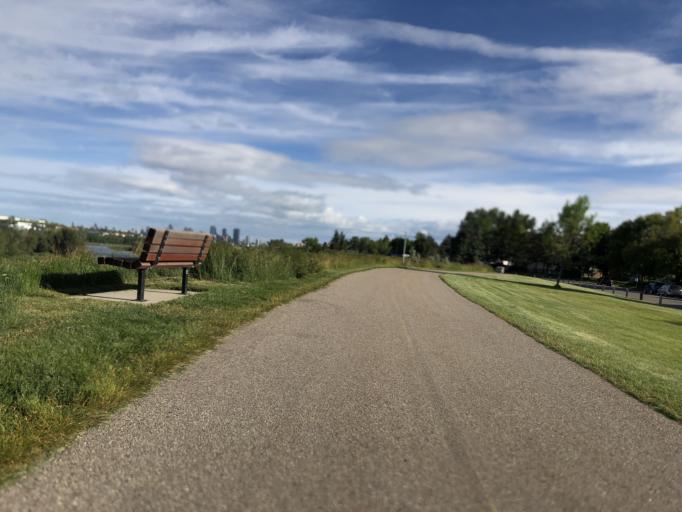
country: CA
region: Alberta
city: Calgary
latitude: 50.9891
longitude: -114.0196
